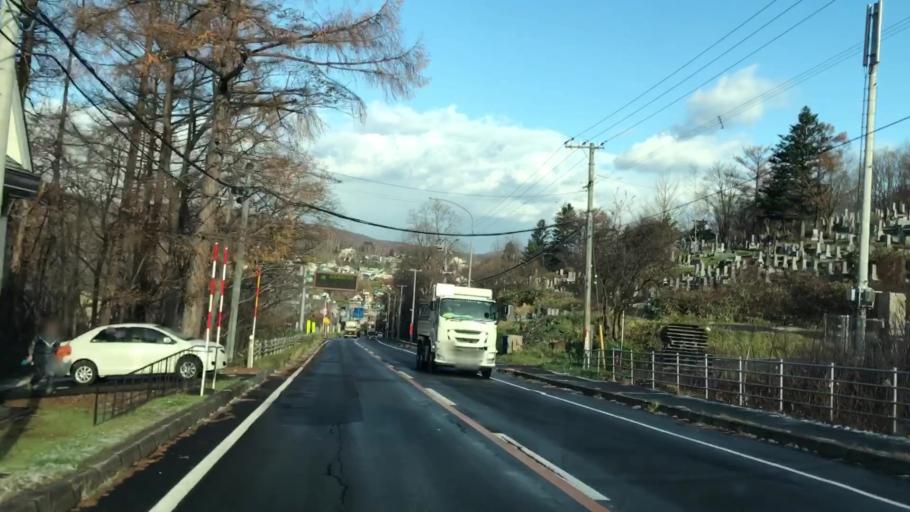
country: JP
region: Hokkaido
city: Otaru
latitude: 43.1646
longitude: 140.9967
